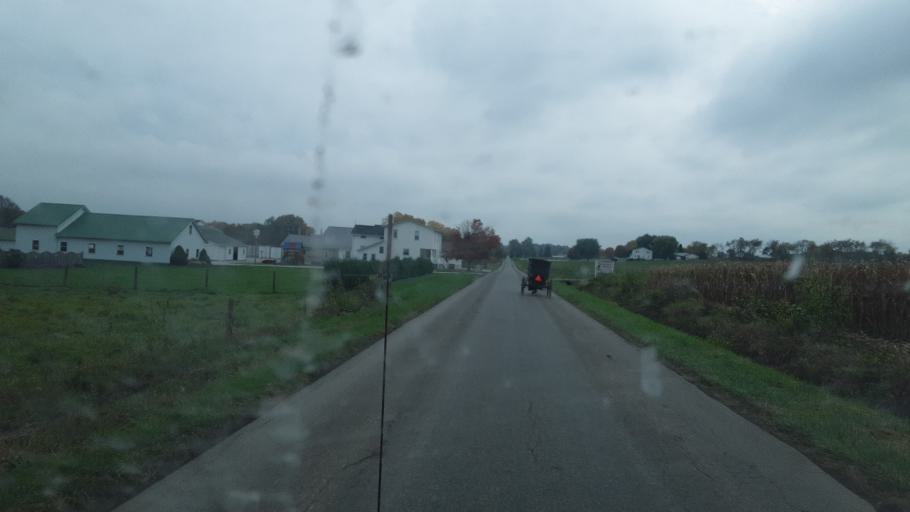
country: US
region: Ohio
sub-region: Wayne County
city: Apple Creek
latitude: 40.7085
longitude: -81.8771
